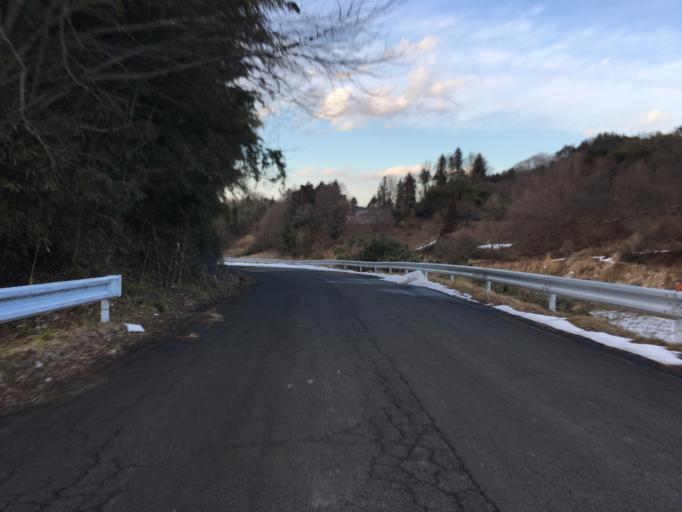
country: JP
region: Fukushima
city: Fukushima-shi
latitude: 37.6413
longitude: 140.5898
